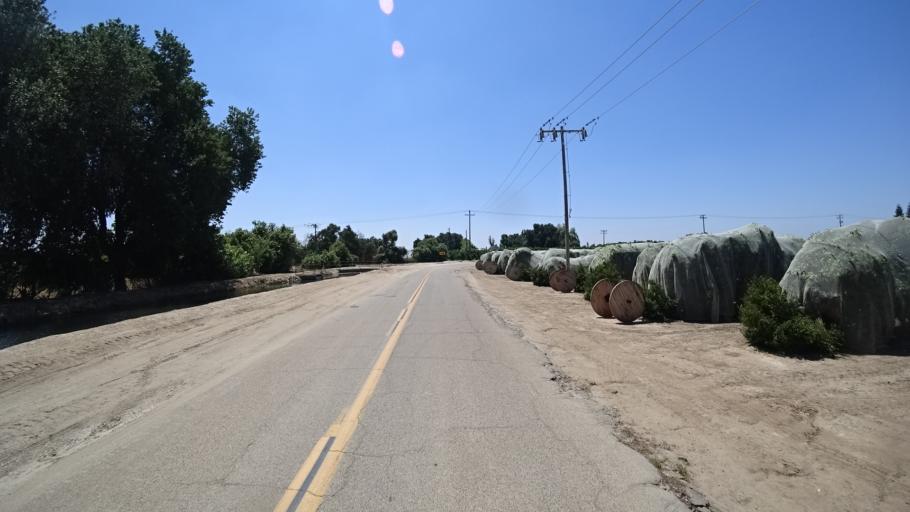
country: US
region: California
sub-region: Fresno County
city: Kingsburg
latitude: 36.4897
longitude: -119.5389
